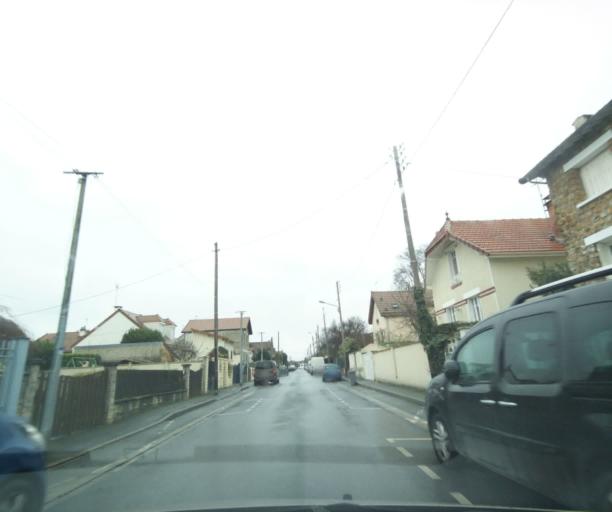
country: FR
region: Ile-de-France
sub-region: Departement du Val-de-Marne
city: Villeneuve-le-Roi
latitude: 48.7363
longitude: 2.4114
